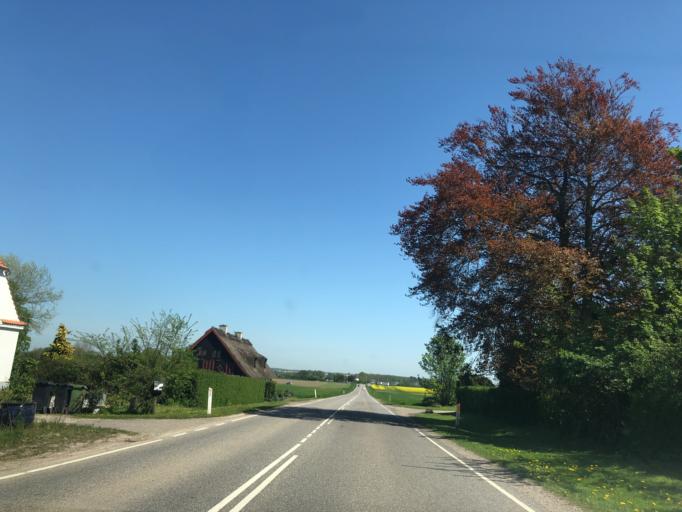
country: DK
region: Zealand
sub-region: Slagelse Kommune
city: Skaelskor
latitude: 55.3018
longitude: 11.2766
